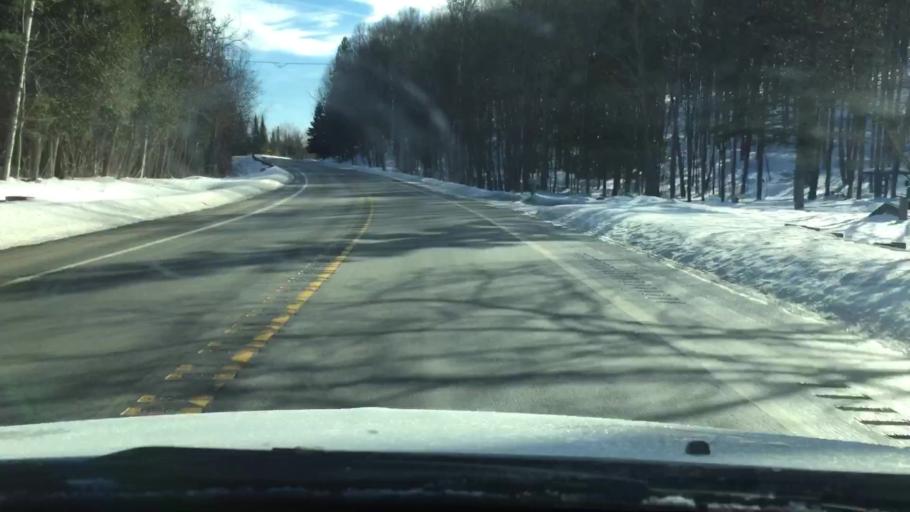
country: US
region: Michigan
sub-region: Antrim County
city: Mancelona
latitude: 45.0002
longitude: -85.0629
